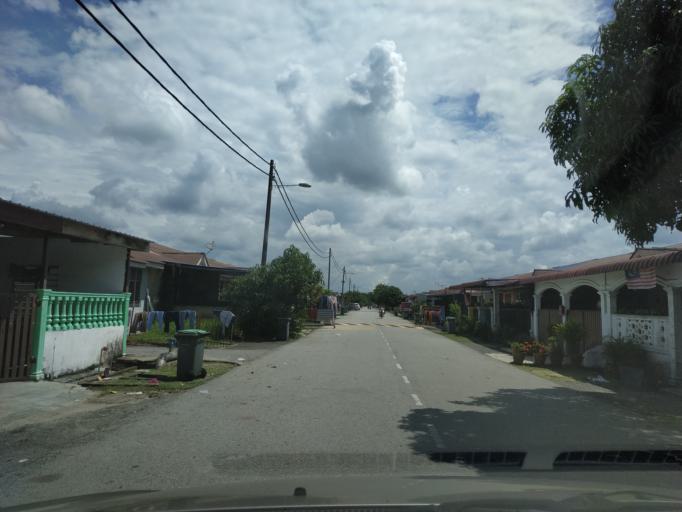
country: MY
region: Perak
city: Parit Buntar
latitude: 5.1398
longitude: 100.5937
